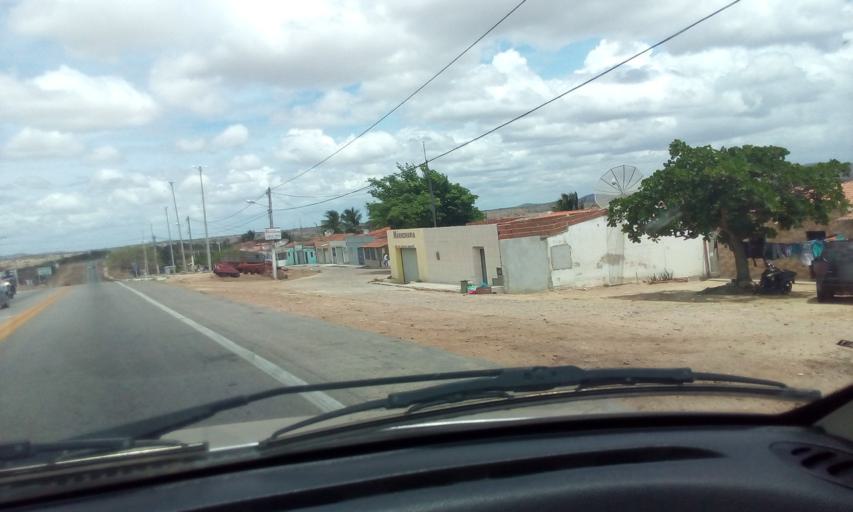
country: BR
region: Rio Grande do Norte
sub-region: Tangara
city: Tangara
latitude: -6.1960
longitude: -35.7965
